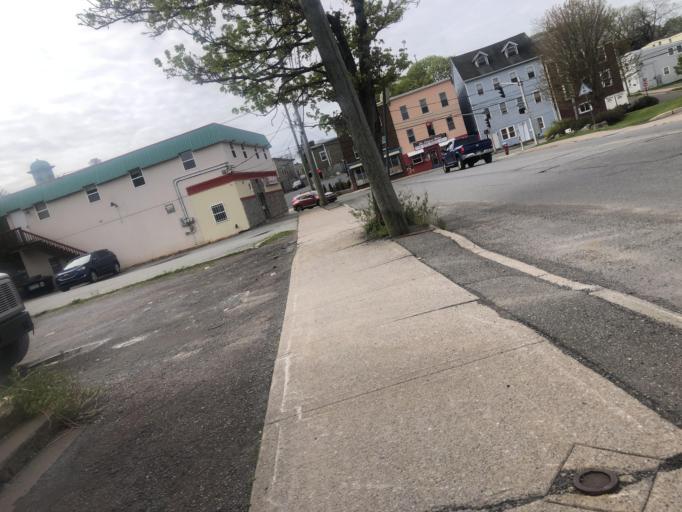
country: CA
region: New Brunswick
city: Saint John
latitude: 45.2759
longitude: -66.0802
